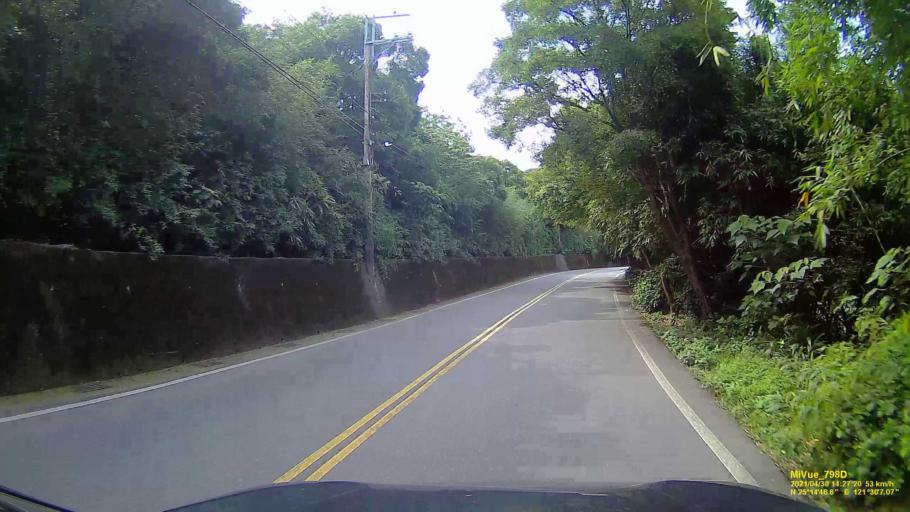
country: TW
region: Taipei
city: Taipei
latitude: 25.2466
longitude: 121.5018
